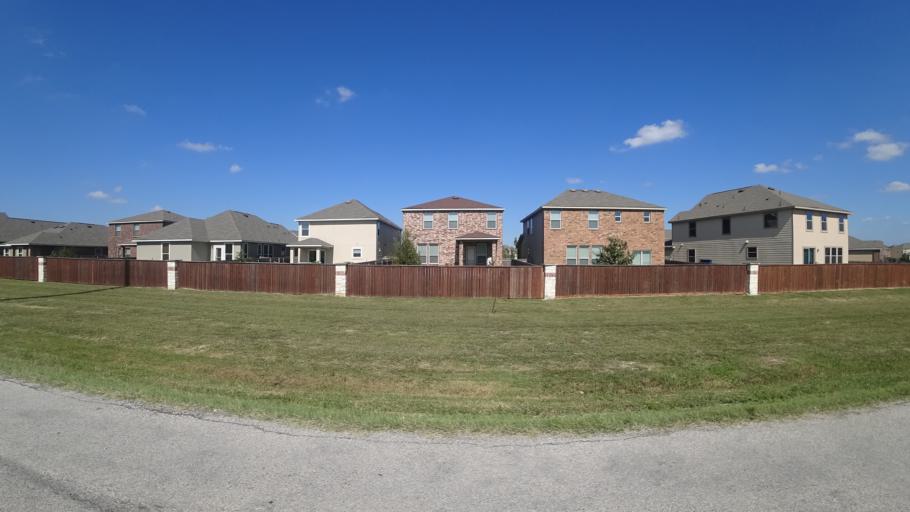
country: US
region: Texas
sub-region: Travis County
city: Manor
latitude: 30.3448
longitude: -97.6194
